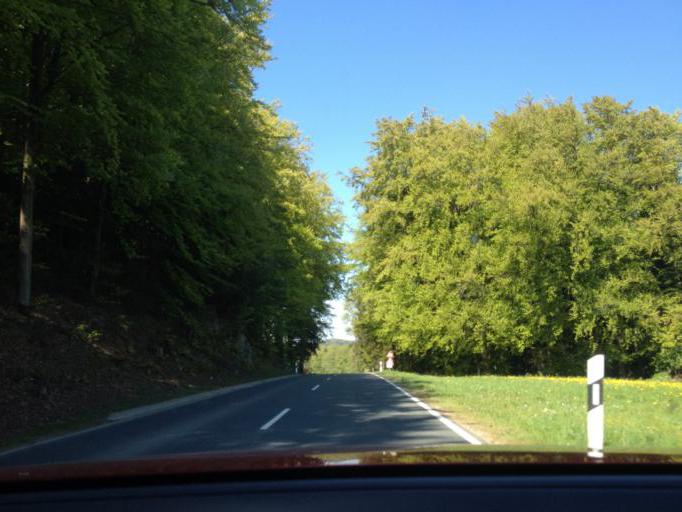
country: DE
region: Bavaria
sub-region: Regierungsbezirk Mittelfranken
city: Kirchensittenbach
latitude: 49.6121
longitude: 11.4257
